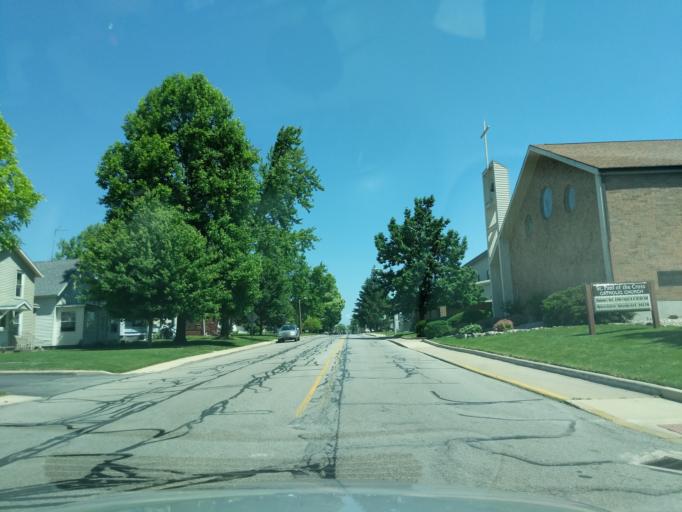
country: US
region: Indiana
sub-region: Whitley County
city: Columbia City
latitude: 41.1538
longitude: -85.4912
